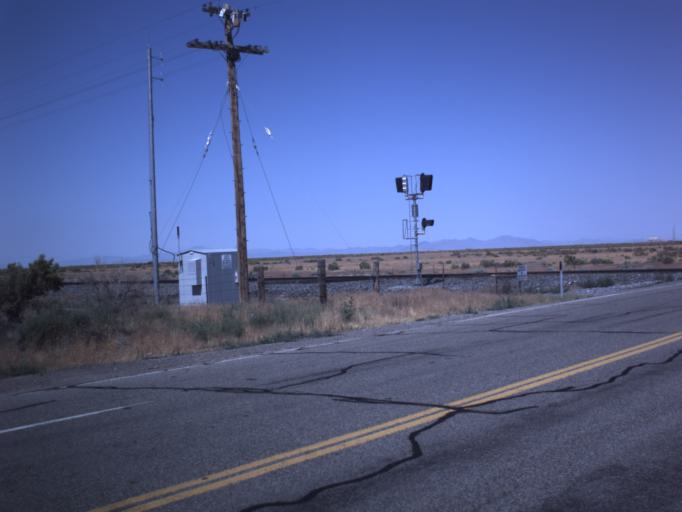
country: US
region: Utah
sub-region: Millard County
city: Delta
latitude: 39.4642
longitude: -112.4368
